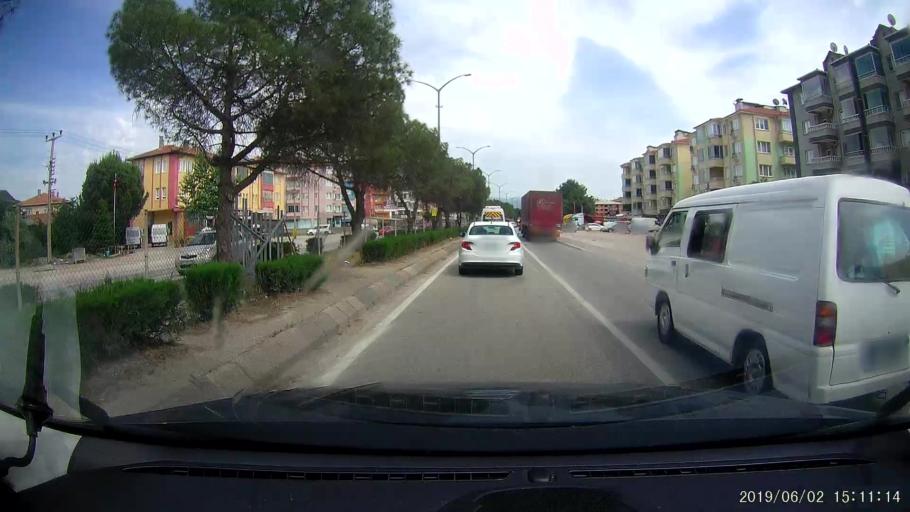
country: TR
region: Corum
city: Osmancik
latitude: 40.9782
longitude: 34.8074
